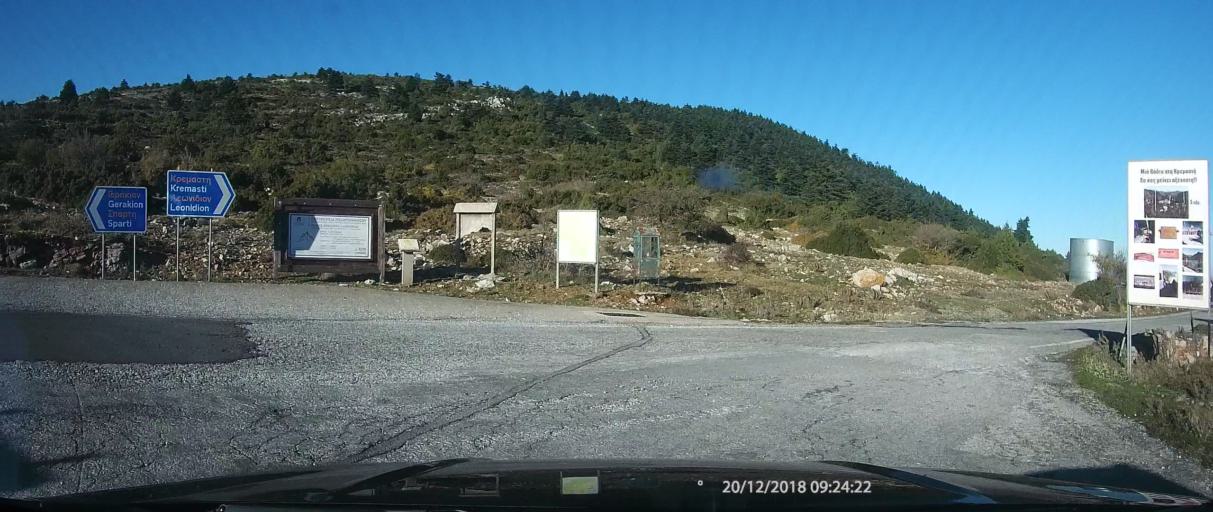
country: GR
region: Peloponnese
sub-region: Nomos Lakonias
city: Molaoi
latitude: 36.9642
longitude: 22.8909
